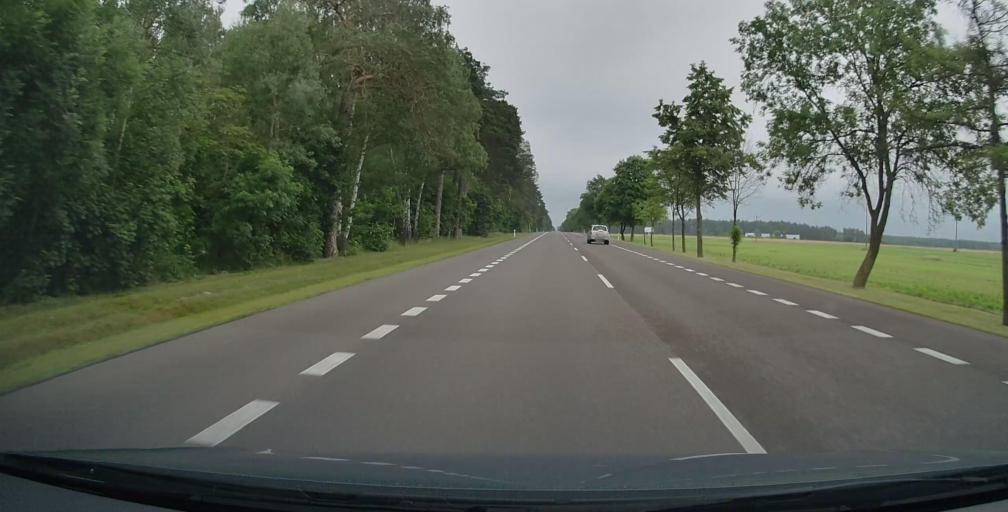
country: PL
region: Lublin Voivodeship
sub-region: Powiat bialski
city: Lesna Podlaska
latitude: 52.0380
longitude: 22.9615
